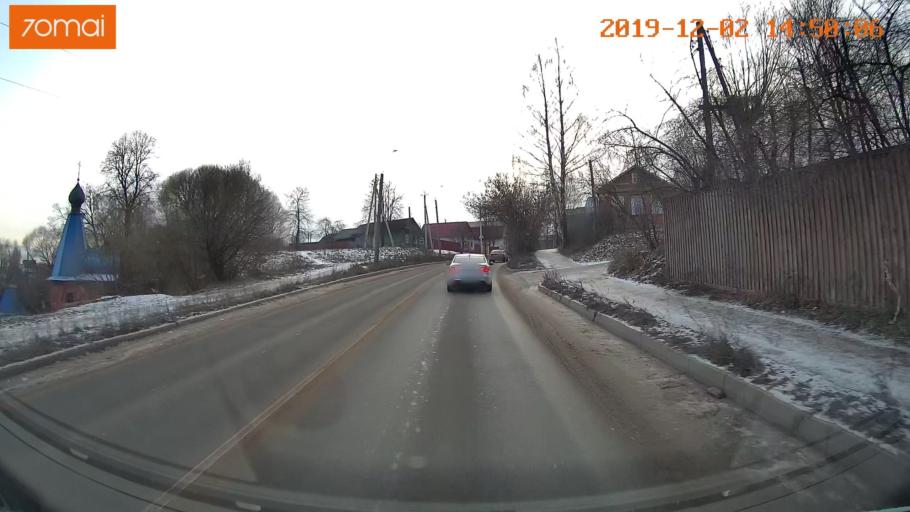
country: RU
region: Ivanovo
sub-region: Gorod Ivanovo
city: Ivanovo
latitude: 56.9821
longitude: 41.0078
